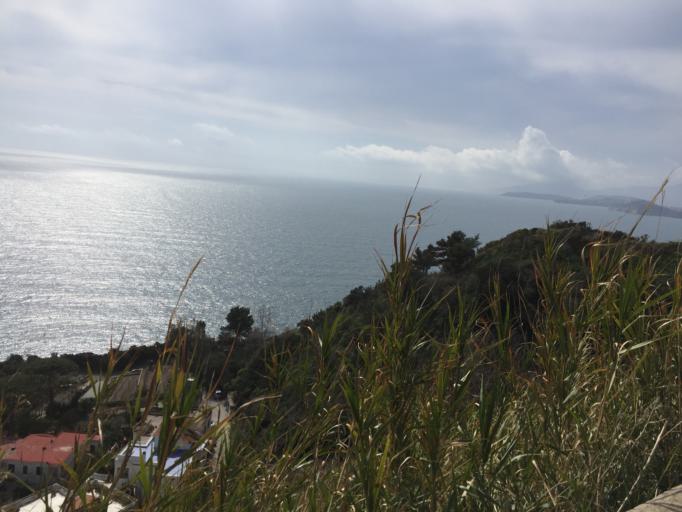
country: IT
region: Campania
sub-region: Provincia di Napoli
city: Bacoli
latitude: 40.7810
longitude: 14.0878
